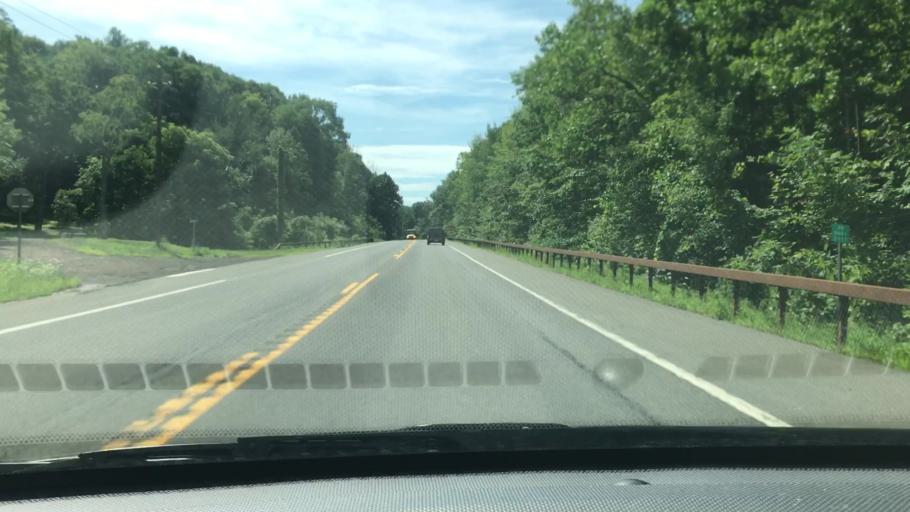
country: US
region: New York
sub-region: Ulster County
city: Shokan
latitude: 41.9868
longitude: -74.2601
